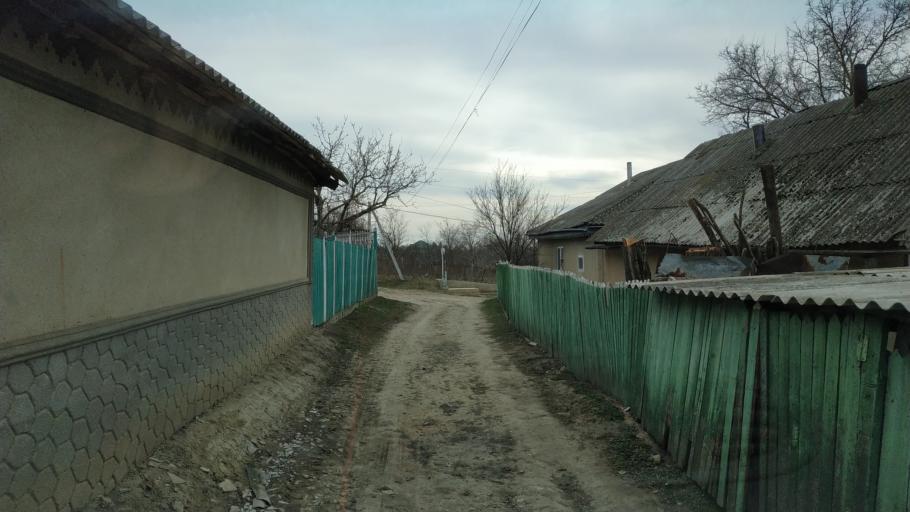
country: MD
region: Hincesti
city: Dancu
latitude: 46.9234
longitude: 28.2750
